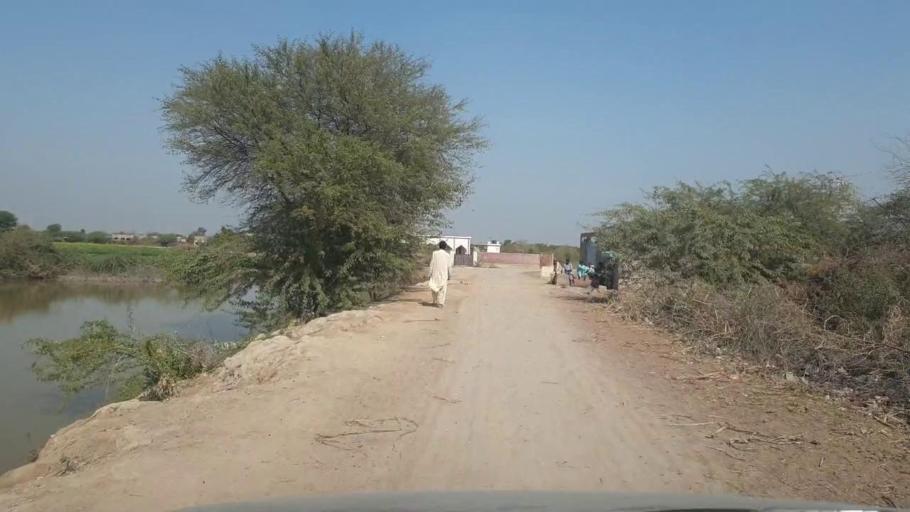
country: PK
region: Sindh
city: Chambar
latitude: 25.2439
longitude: 68.8613
